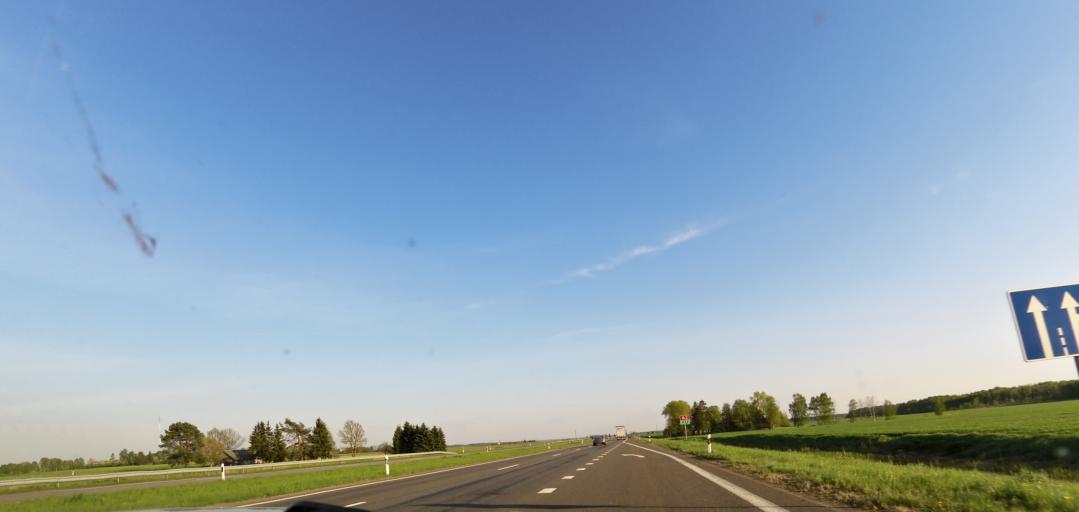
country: LT
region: Vilnius County
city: Ukmerge
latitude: 55.3940
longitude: 24.7021
